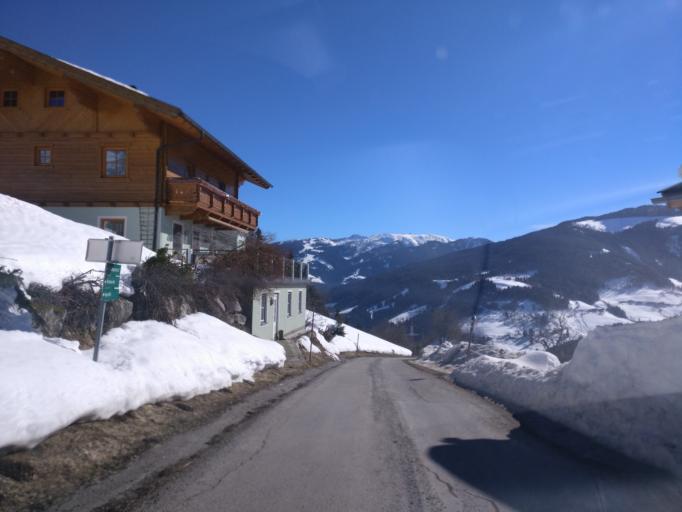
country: AT
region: Salzburg
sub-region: Politischer Bezirk Sankt Johann im Pongau
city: Sankt Johann im Pongau
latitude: 47.3372
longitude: 13.2274
